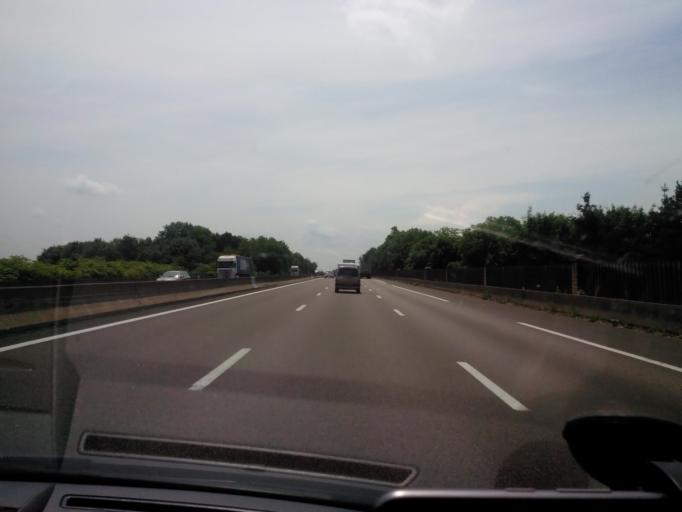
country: FR
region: Bourgogne
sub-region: Departement de Saone-et-Loire
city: Chatenoy-le-Royal
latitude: 46.7982
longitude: 4.8239
